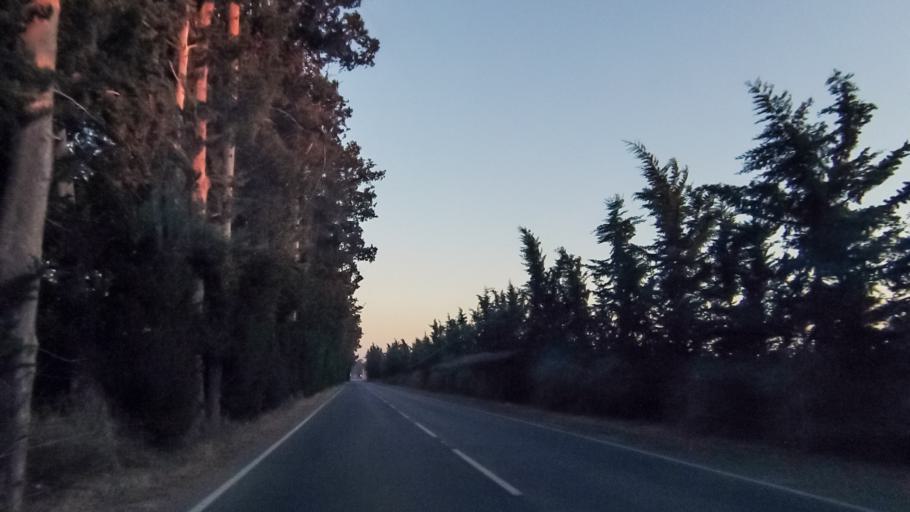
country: CY
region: Larnaka
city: Kolossi
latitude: 34.6480
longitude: 32.9431
